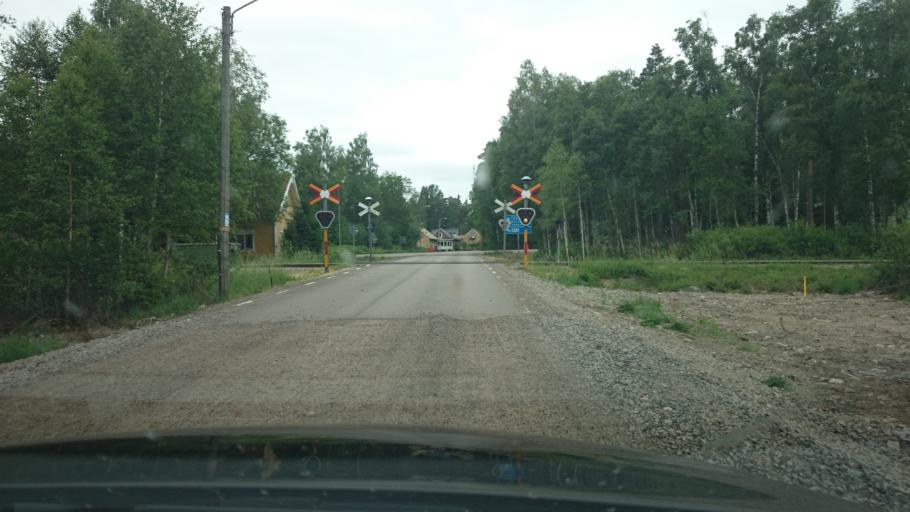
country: SE
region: Halland
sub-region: Hylte Kommun
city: Torup
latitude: 56.9638
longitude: 13.1479
